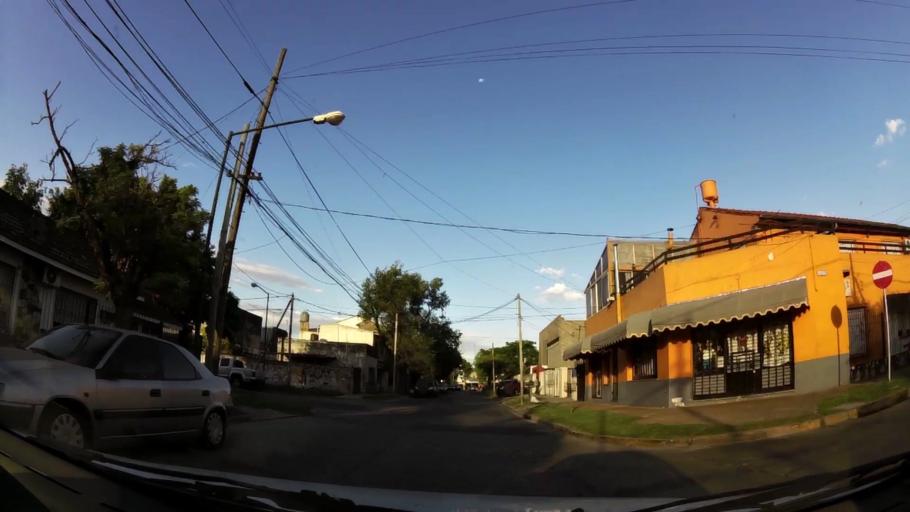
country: AR
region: Buenos Aires
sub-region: Partido de San Isidro
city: San Isidro
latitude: -34.4671
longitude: -58.5451
